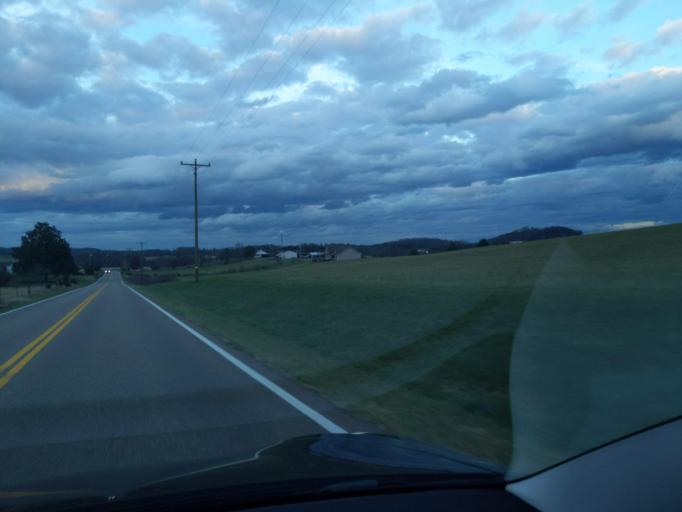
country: US
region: Tennessee
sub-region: Jefferson County
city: Dandridge
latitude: 36.0751
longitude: -83.3822
